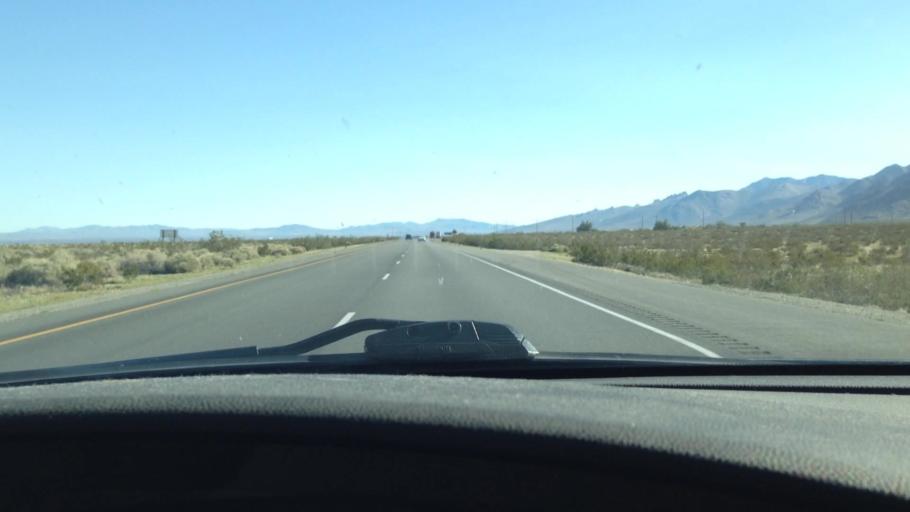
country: US
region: California
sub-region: Kern County
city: Inyokern
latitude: 35.8471
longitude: -117.8756
